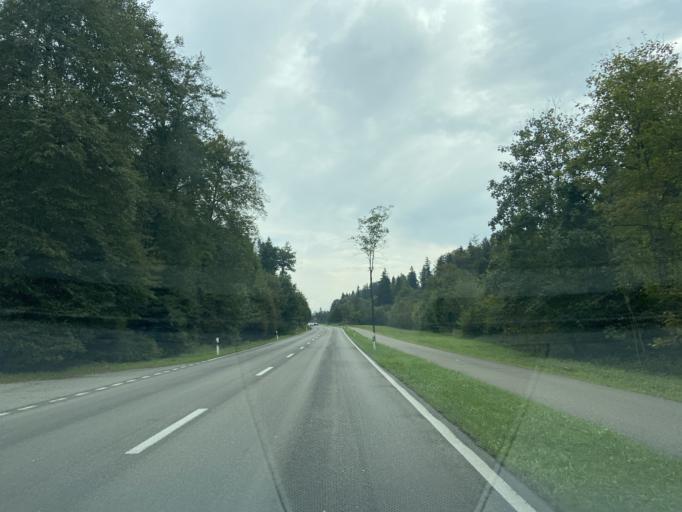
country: CH
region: Zurich
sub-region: Bezirk Pfaeffikon
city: Effretikon / Watt
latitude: 47.4278
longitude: 8.7089
